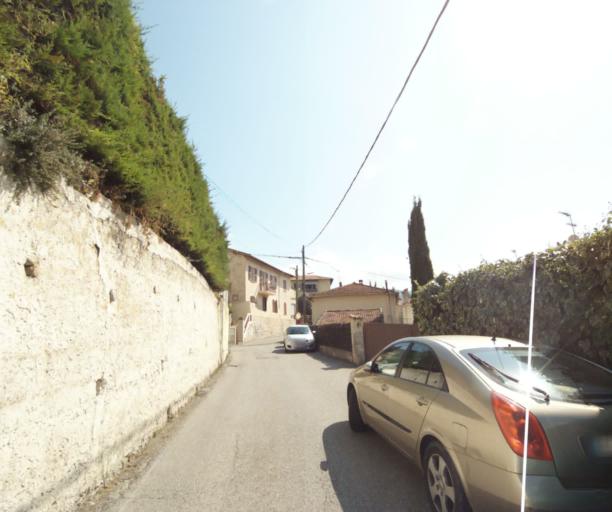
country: FR
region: Provence-Alpes-Cote d'Azur
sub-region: Departement des Alpes-Maritimes
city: Drap
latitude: 43.7563
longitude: 7.3222
